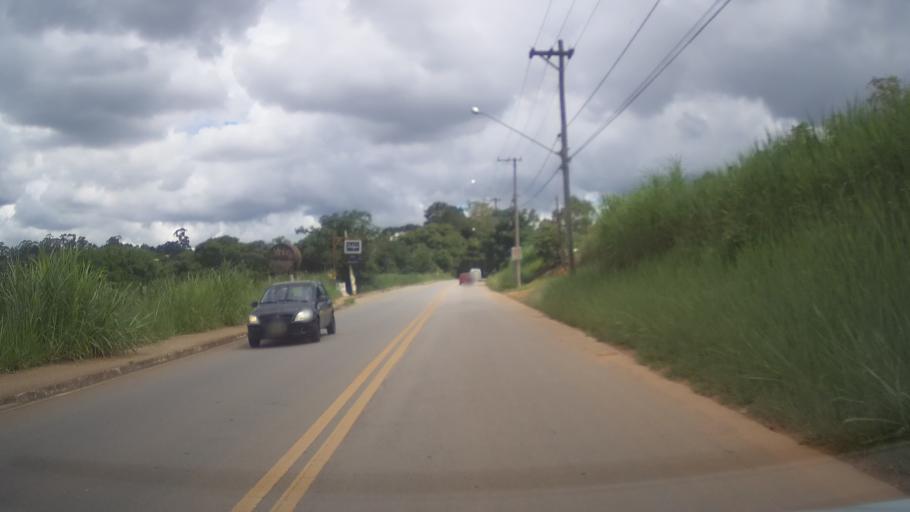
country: BR
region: Sao Paulo
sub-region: Varzea Paulista
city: Varzea Paulista
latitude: -23.1722
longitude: -46.8151
